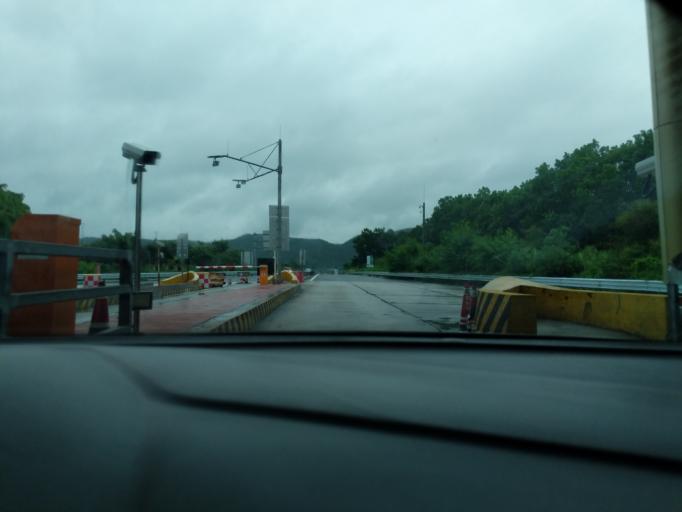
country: CN
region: Guangdong
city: Pingshi
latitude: 22.2386
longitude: 112.3057
